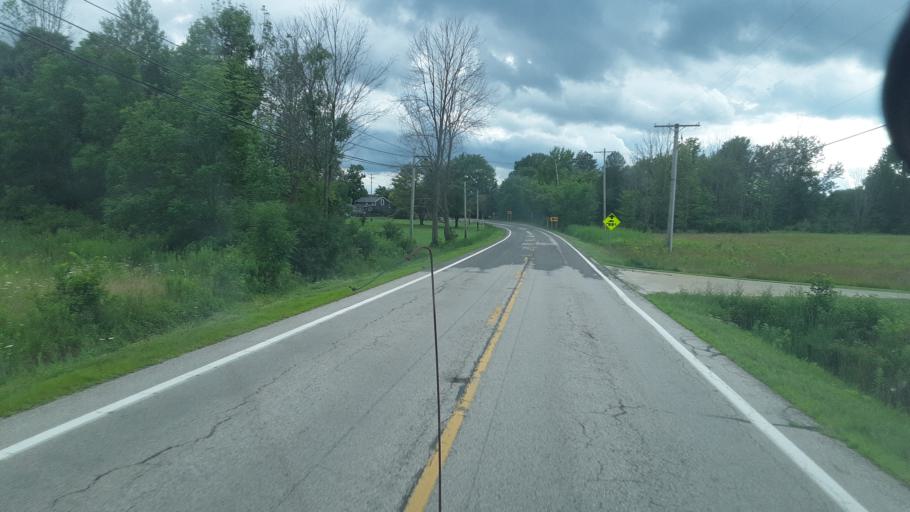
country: US
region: Ohio
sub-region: Ashtabula County
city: Jefferson
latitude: 41.7159
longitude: -80.7794
